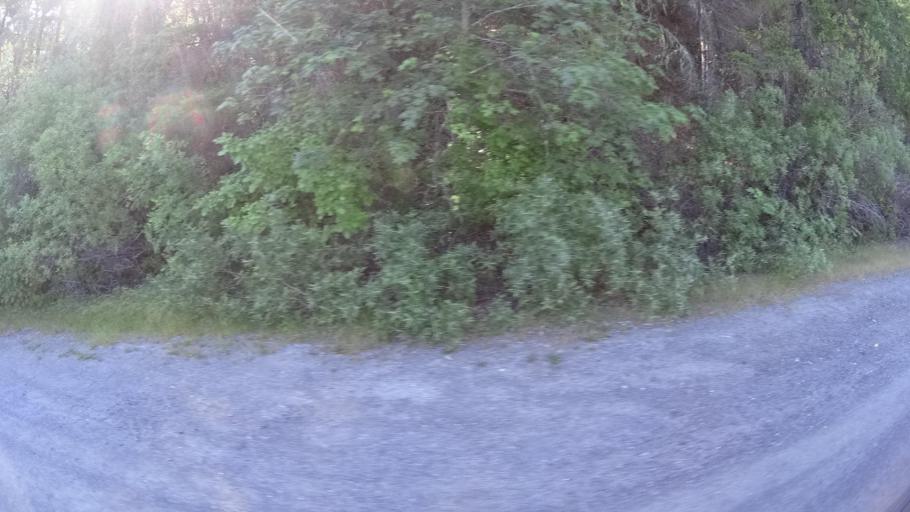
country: US
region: California
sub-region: Lake County
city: Upper Lake
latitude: 39.4082
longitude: -122.9822
